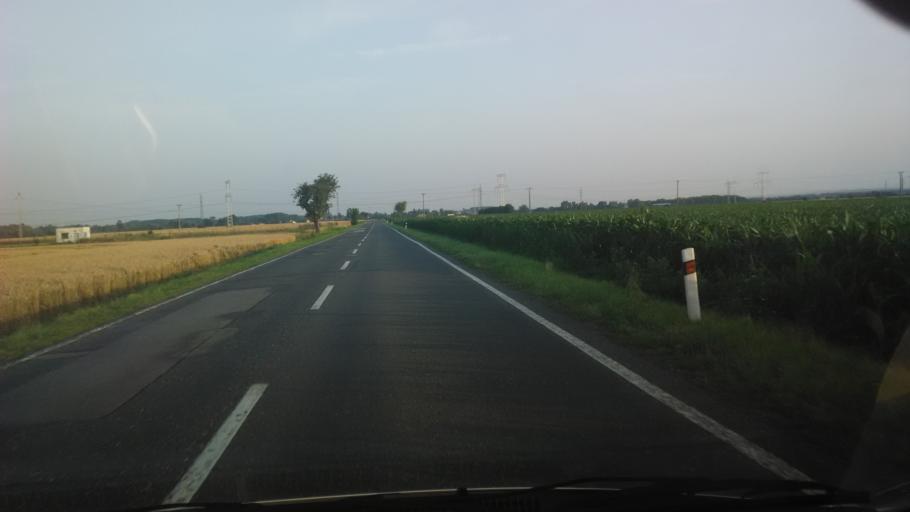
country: SK
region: Nitriansky
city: Tlmace
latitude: 48.2240
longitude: 18.5194
